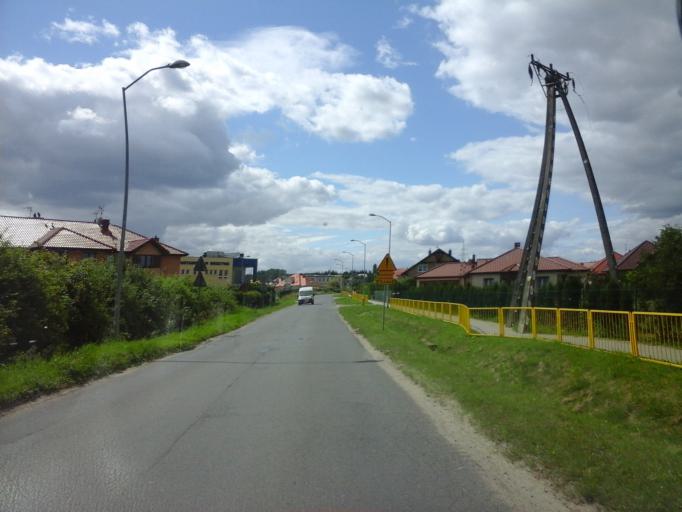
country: PL
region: West Pomeranian Voivodeship
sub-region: Powiat policki
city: Przeclaw
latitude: 53.4277
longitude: 14.4629
